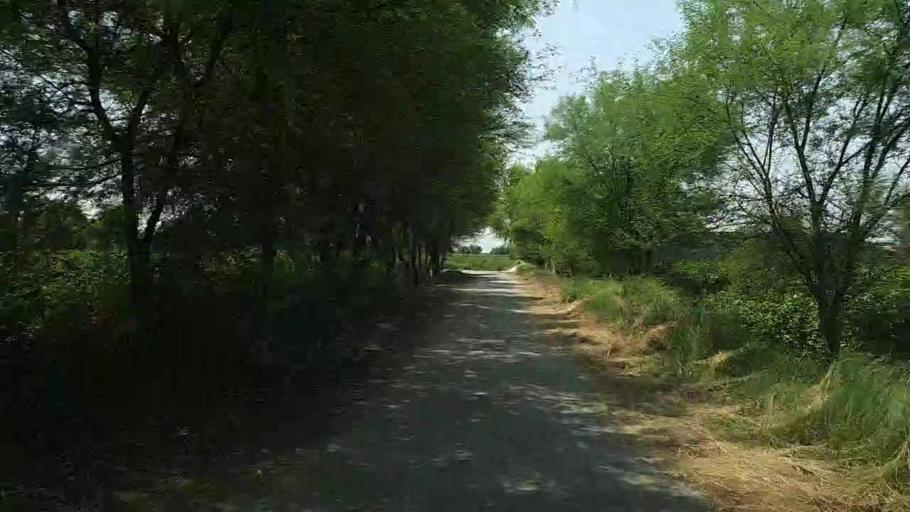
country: PK
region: Sindh
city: Ubauro
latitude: 28.1518
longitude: 69.7689
